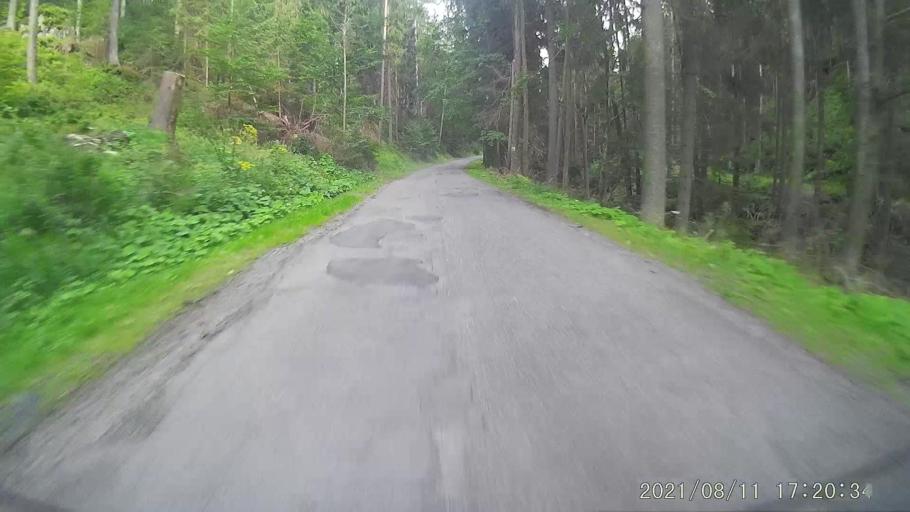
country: PL
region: Lower Silesian Voivodeship
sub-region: Powiat klodzki
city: Polanica-Zdroj
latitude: 50.3080
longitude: 16.5107
